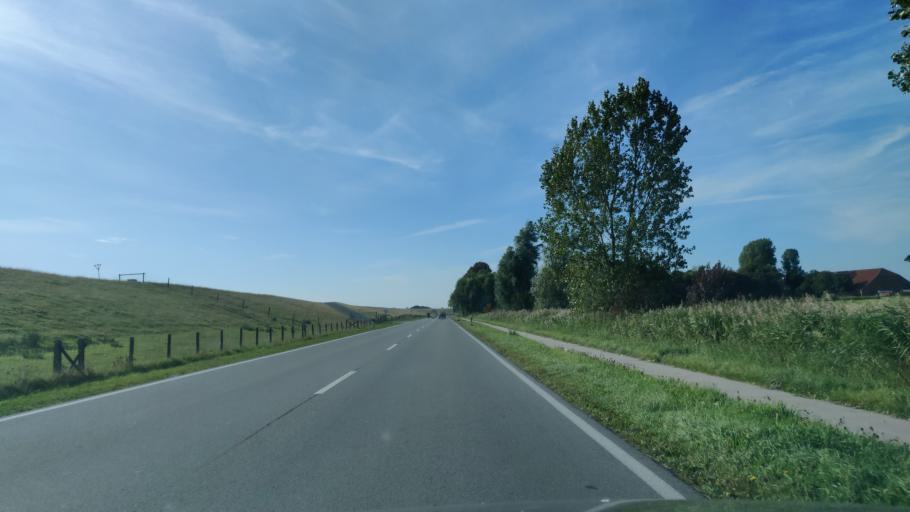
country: DE
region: Lower Saxony
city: Leer
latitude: 53.2333
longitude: 7.4203
